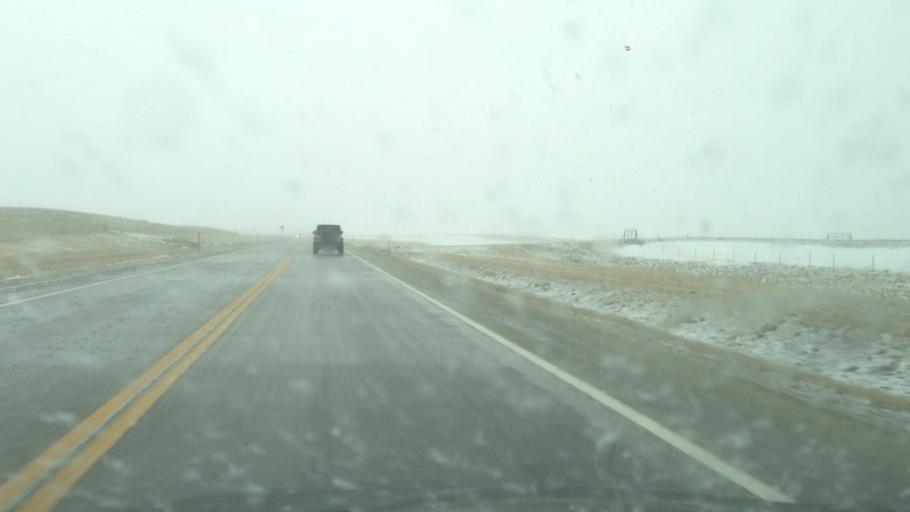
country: US
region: Colorado
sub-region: Park County
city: Castle Pines North
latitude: 39.4846
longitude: -104.8555
